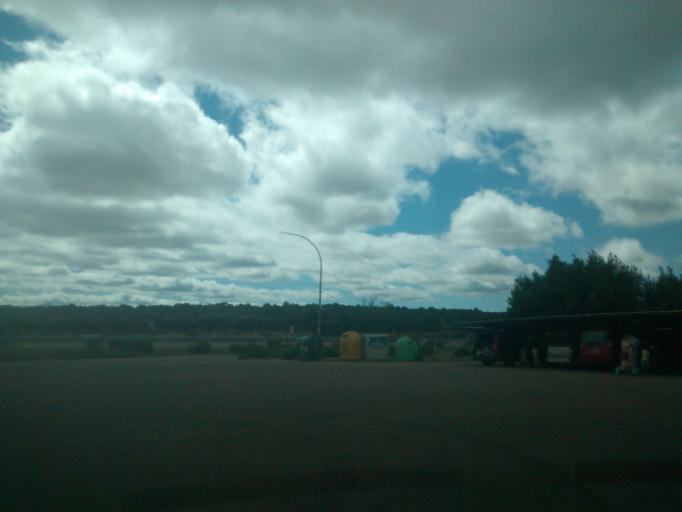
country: ES
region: Castille and Leon
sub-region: Provincia de Salamanca
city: Tenebron
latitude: 40.6636
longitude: -6.4380
